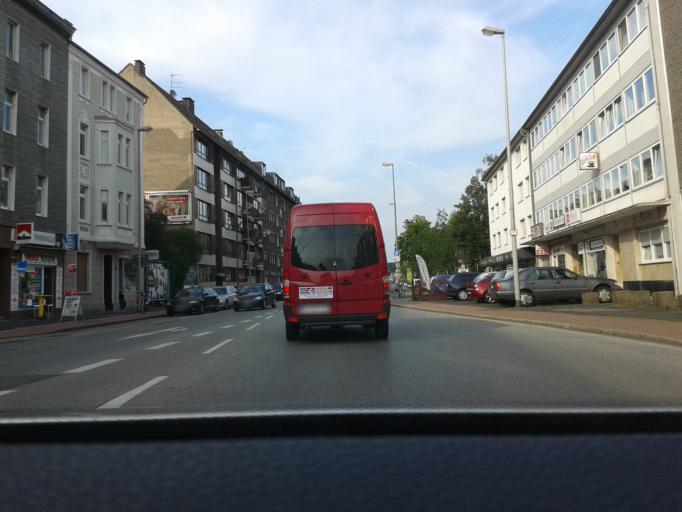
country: DE
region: North Rhine-Westphalia
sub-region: Regierungsbezirk Dusseldorf
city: Duisburg
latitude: 51.4215
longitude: 6.7850
